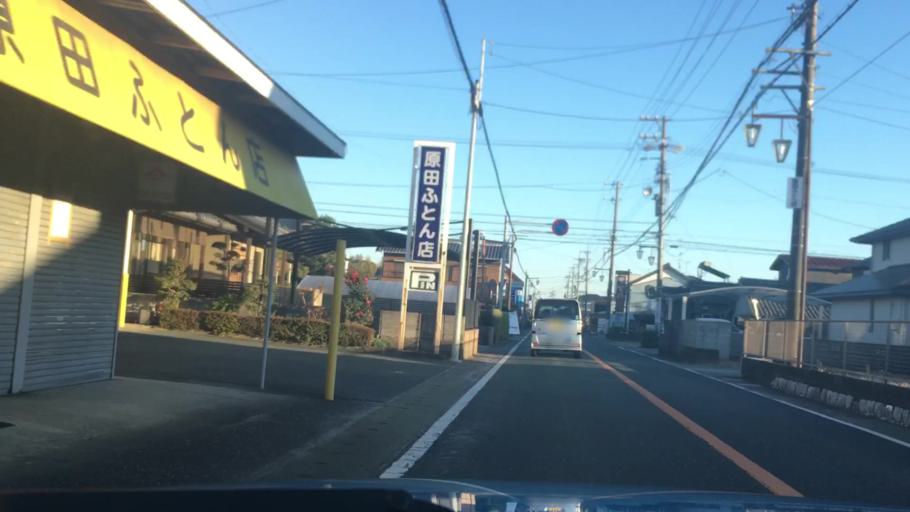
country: JP
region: Shizuoka
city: Hamamatsu
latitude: 34.7391
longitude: 137.6819
